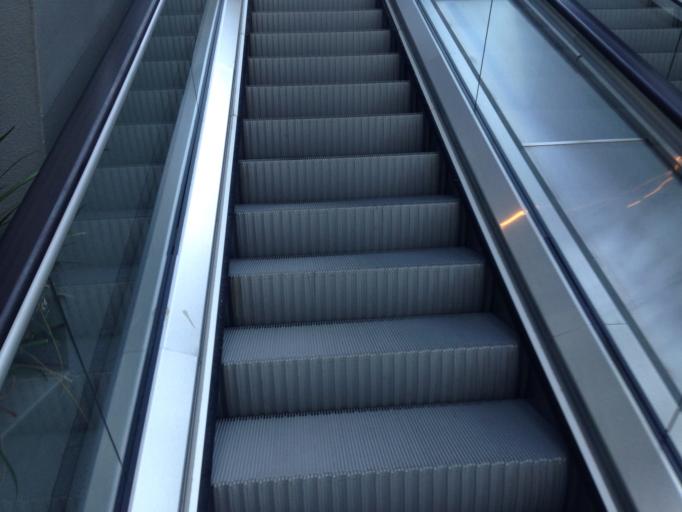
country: AU
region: New South Wales
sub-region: Willoughby
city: Chatswood
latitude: -33.7960
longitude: 151.1804
